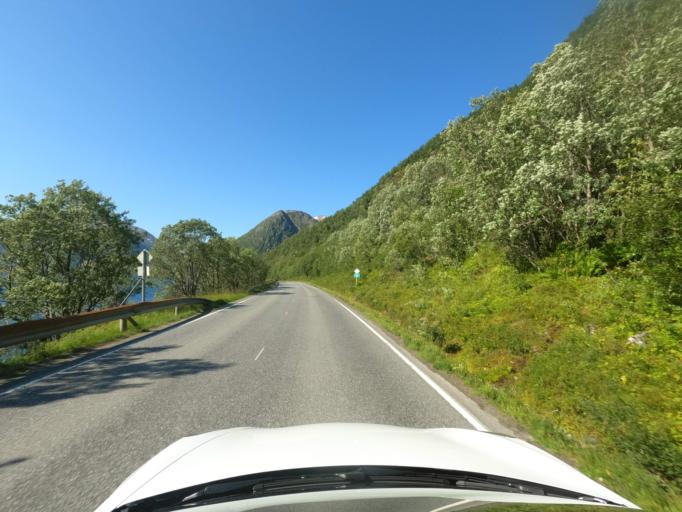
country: NO
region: Nordland
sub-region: Lodingen
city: Lodingen
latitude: 68.5622
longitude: 15.7846
